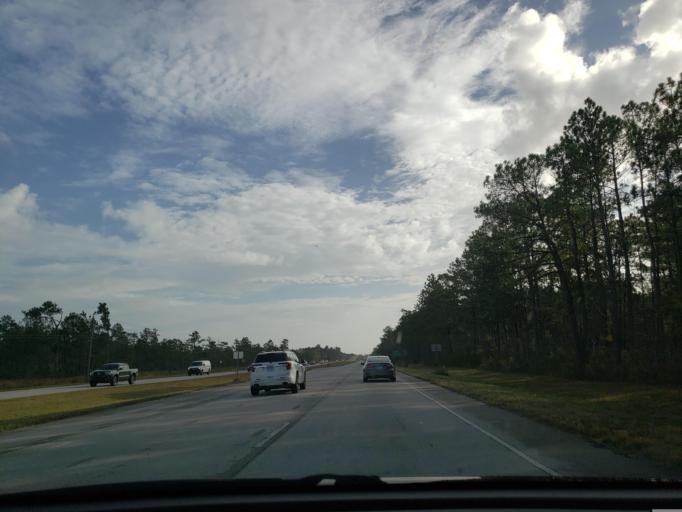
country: US
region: North Carolina
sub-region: Onslow County
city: Sneads Ferry
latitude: 34.6058
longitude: -77.4827
